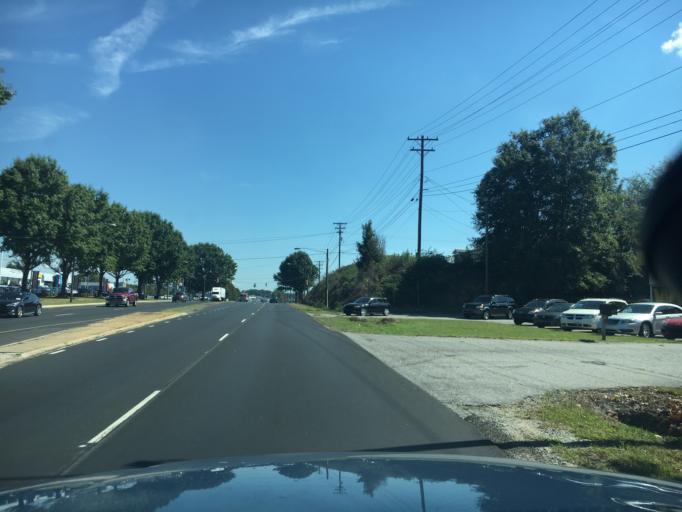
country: US
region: North Carolina
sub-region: Catawba County
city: Hickory
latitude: 35.7116
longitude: -81.3262
